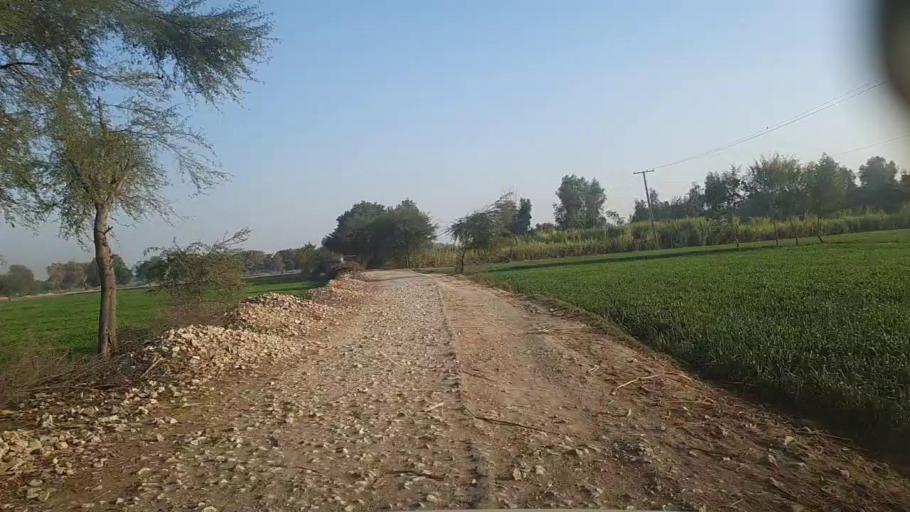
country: PK
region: Sindh
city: Khairpur
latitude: 28.0738
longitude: 69.7388
